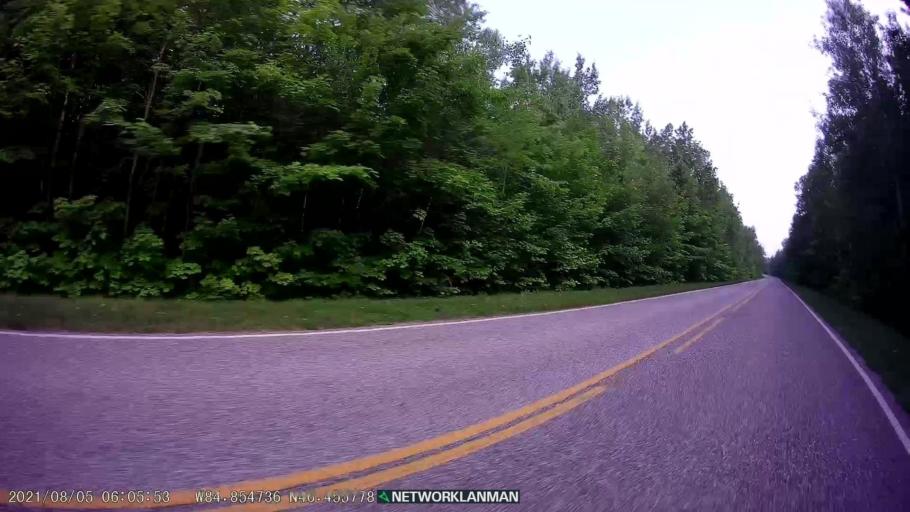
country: US
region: Michigan
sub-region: Chippewa County
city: Sault Ste. Marie
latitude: 46.4561
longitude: -84.8549
